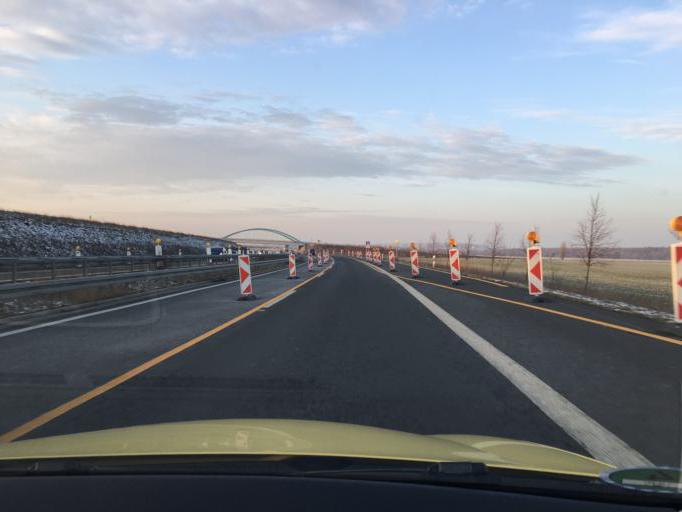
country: DE
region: Saxony
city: Borna
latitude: 51.1270
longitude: 12.5183
